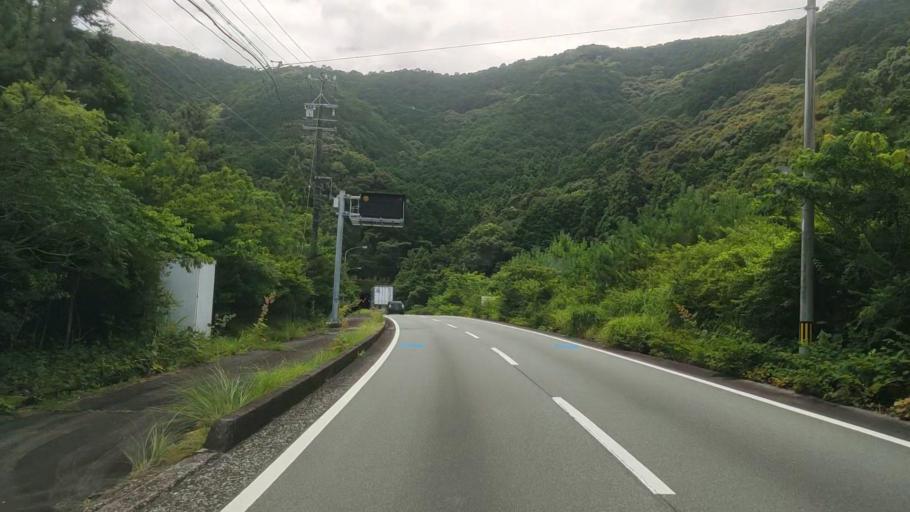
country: JP
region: Mie
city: Owase
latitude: 34.2562
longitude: 136.4546
